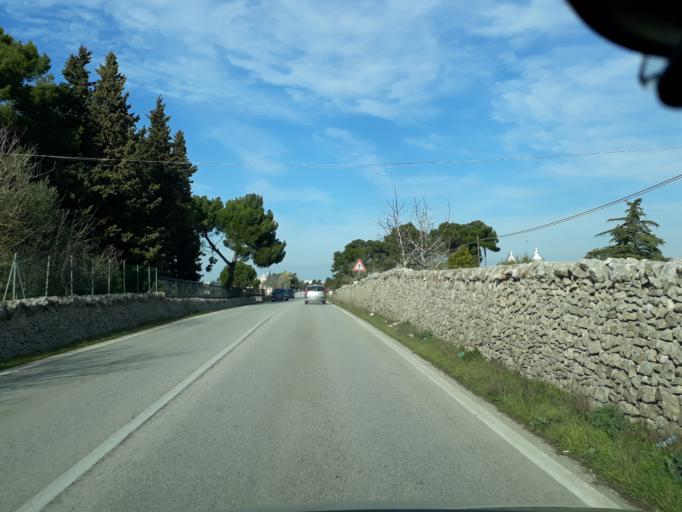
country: IT
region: Apulia
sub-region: Provincia di Taranto
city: Martina Franca
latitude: 40.7224
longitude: 17.3327
